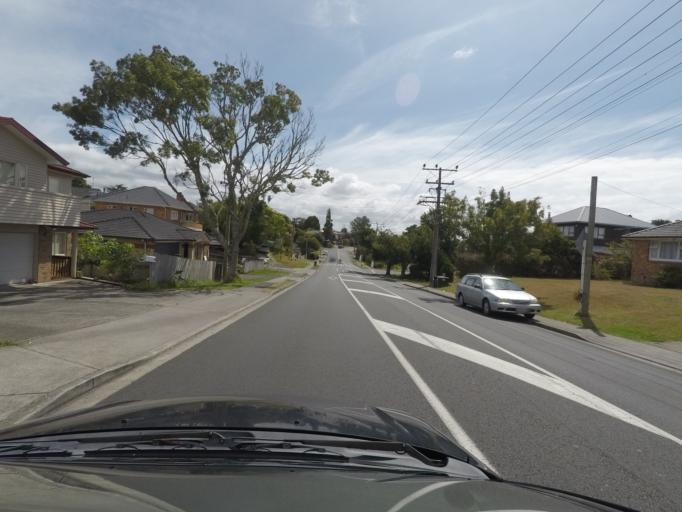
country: NZ
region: Auckland
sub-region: Auckland
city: Waitakere
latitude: -36.9034
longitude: 174.6689
